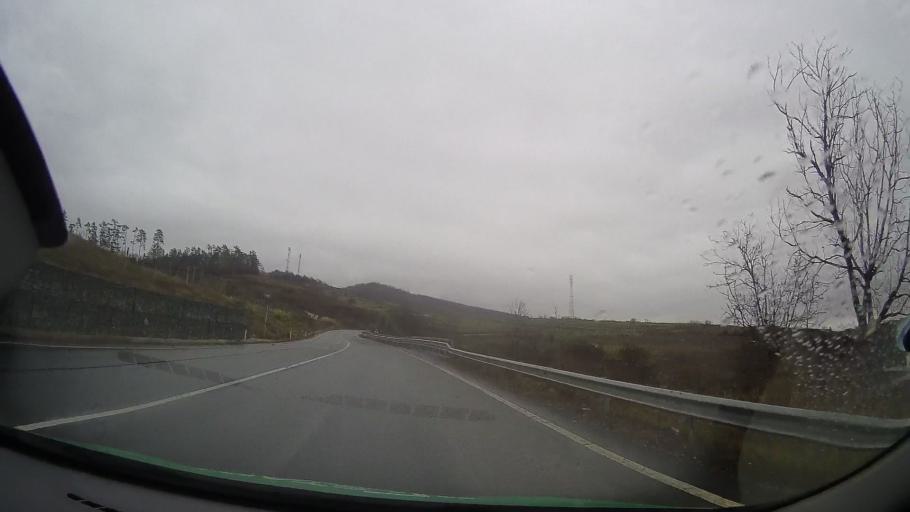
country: RO
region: Bistrita-Nasaud
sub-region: Comuna Teaca
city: Teaca
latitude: 46.9016
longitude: 24.5062
